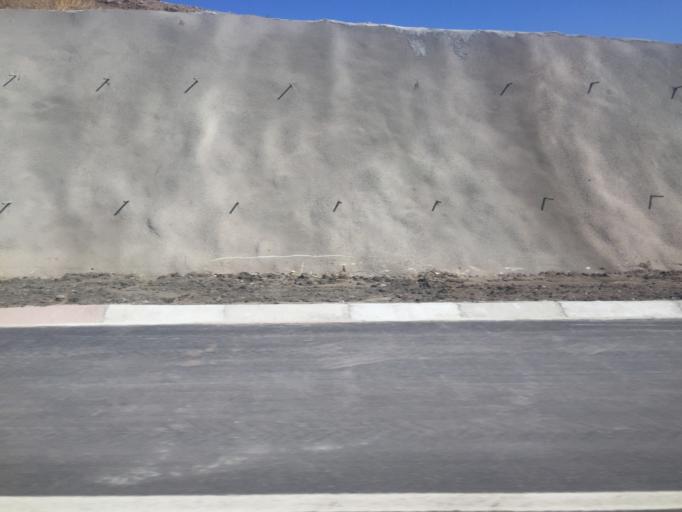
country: TR
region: Bursa
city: Mahmudiye
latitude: 40.2653
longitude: 28.6493
